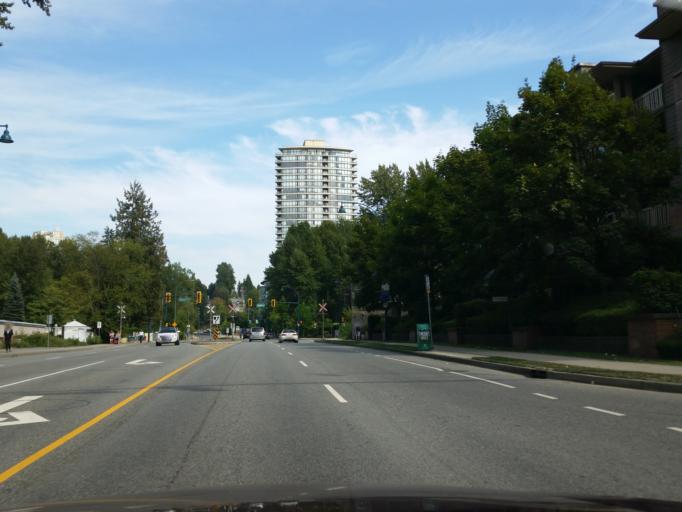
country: CA
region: British Columbia
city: Port Moody
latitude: 49.2805
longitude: -122.8332
